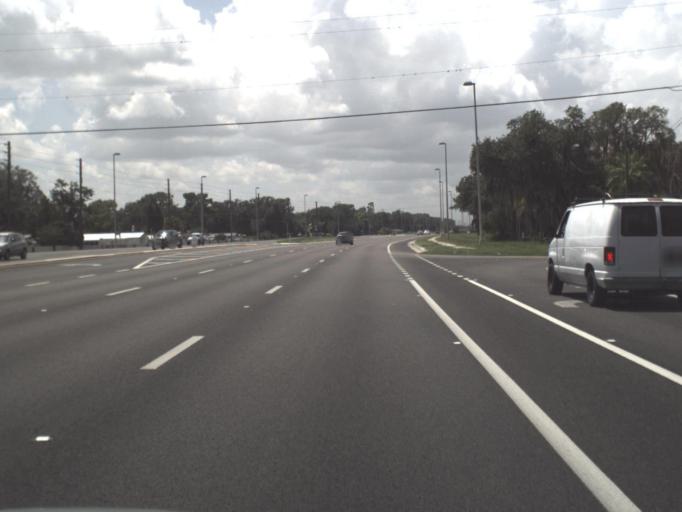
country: US
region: Florida
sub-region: Hillsborough County
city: Riverview
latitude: 27.8467
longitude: -82.3269
